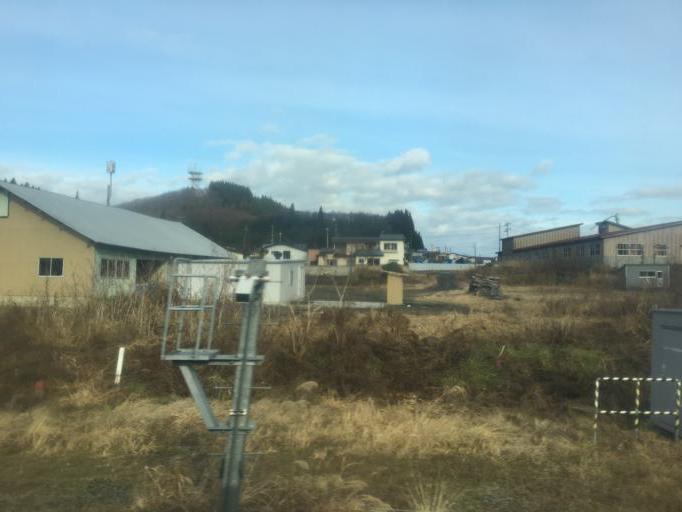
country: JP
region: Akita
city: Takanosu
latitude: 40.2712
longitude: 140.4512
